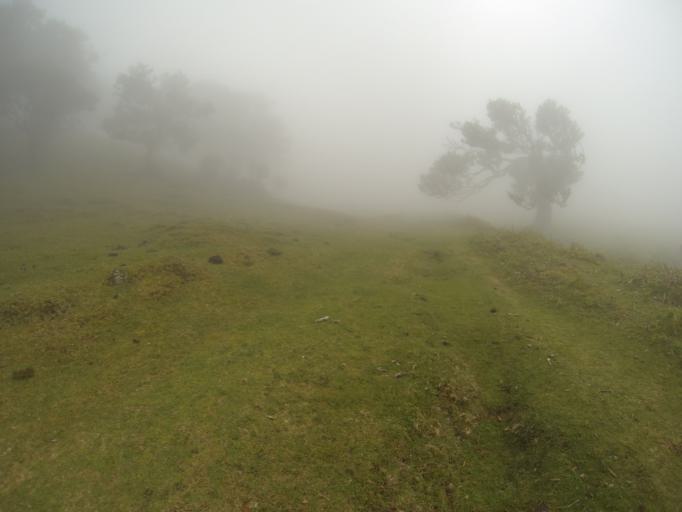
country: PT
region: Madeira
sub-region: Porto Moniz
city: Porto Moniz
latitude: 32.8114
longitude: -17.1417
